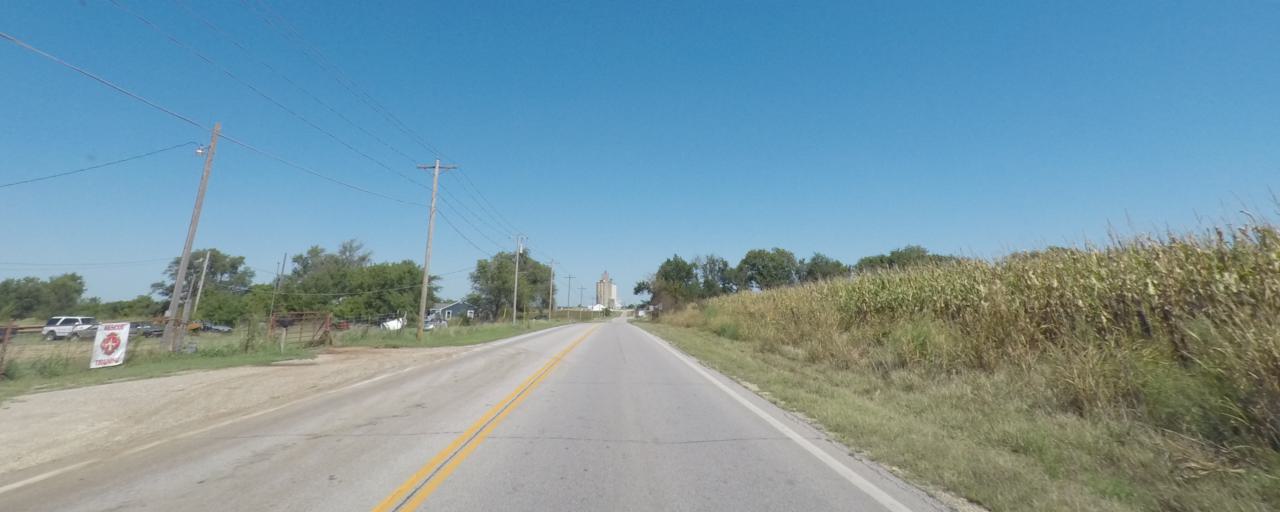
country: US
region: Kansas
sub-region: Sumner County
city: Wellington
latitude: 37.2957
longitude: -97.3940
